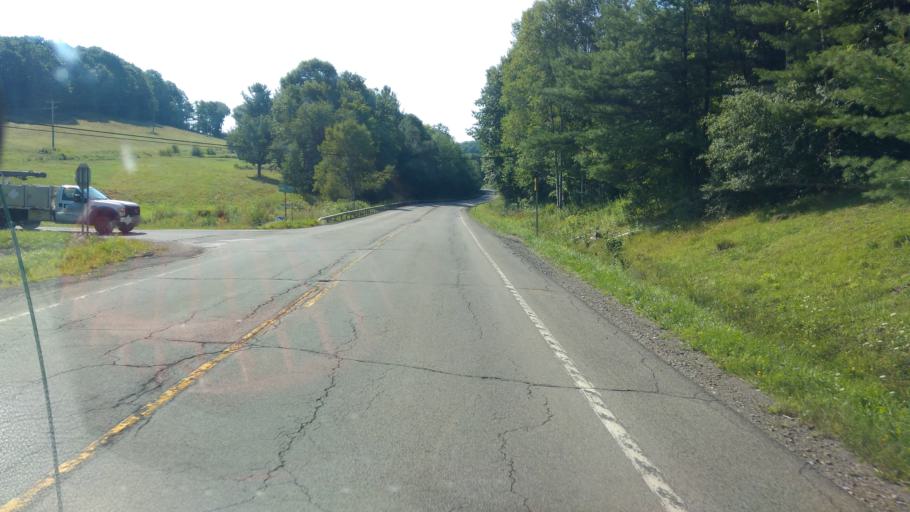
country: US
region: New York
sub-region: Allegany County
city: Cuba
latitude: 42.1818
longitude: -78.2567
